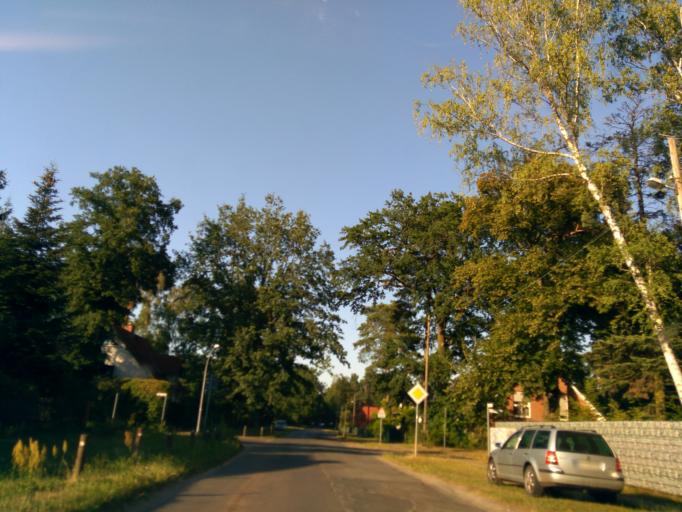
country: DE
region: Brandenburg
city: Falkensee
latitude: 52.5827
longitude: 13.0778
